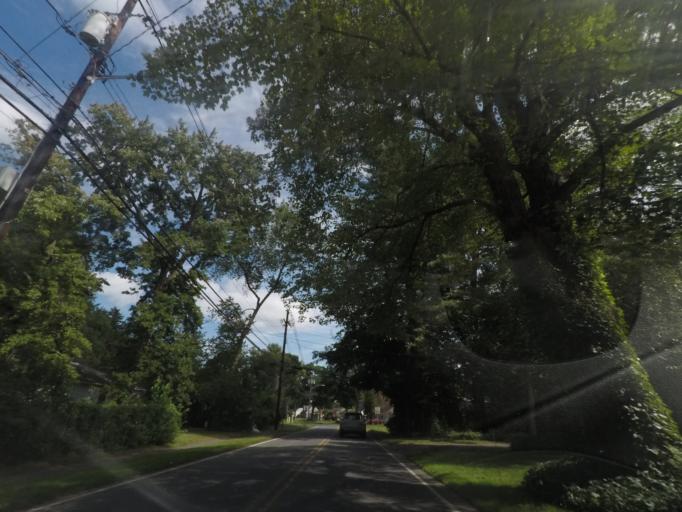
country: US
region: New York
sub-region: Albany County
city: Delmar
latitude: 42.6220
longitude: -73.8145
